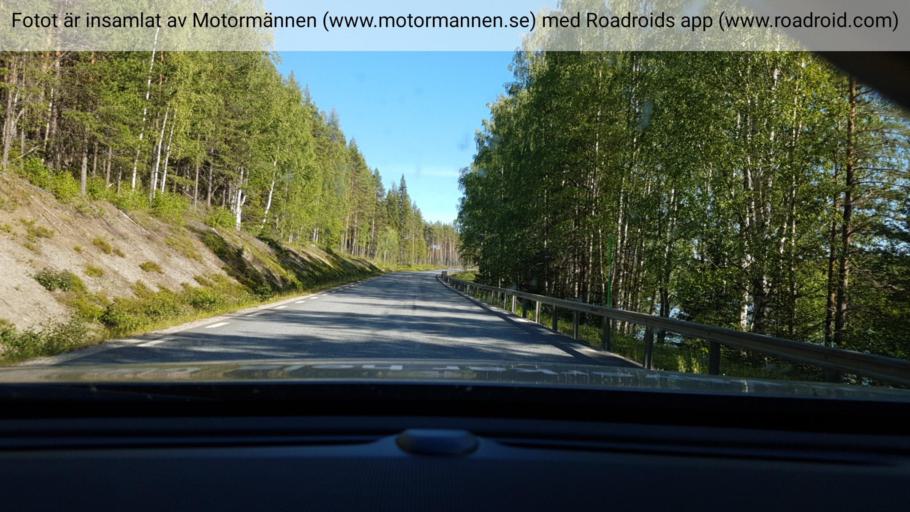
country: SE
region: Vaesterbotten
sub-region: Lycksele Kommun
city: Lycksele
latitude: 64.4172
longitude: 19.0091
